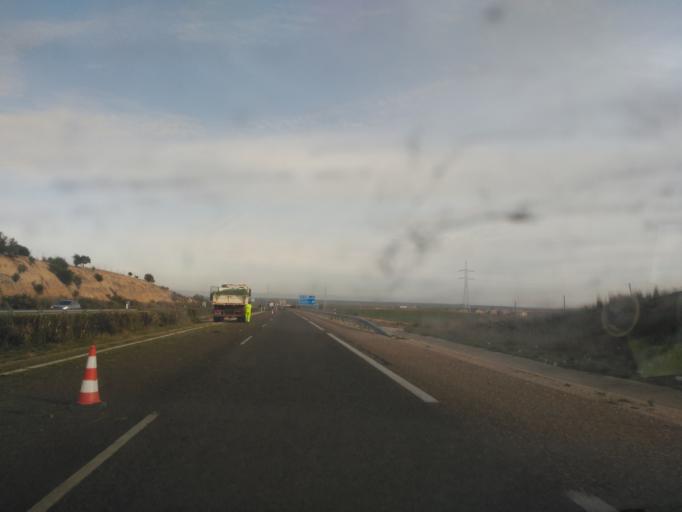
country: ES
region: Castille and Leon
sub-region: Provincia de Salamanca
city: Castellanos de Moriscos
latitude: 41.0074
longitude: -5.5987
